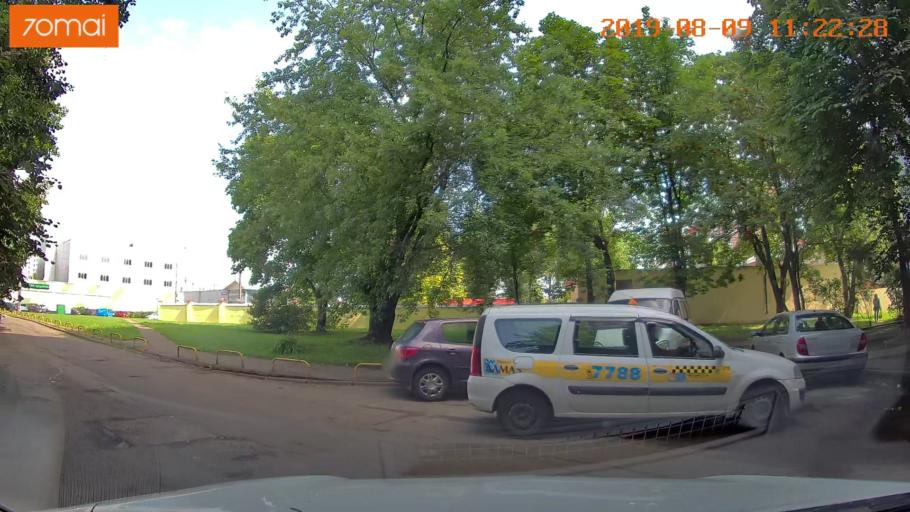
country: BY
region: Minsk
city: Minsk
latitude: 53.8831
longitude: 27.5410
